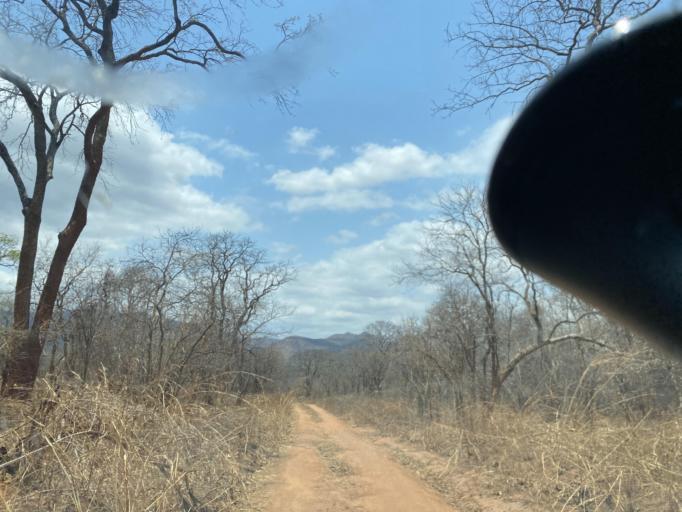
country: ZM
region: Lusaka
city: Luangwa
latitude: -15.1747
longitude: 29.7129
